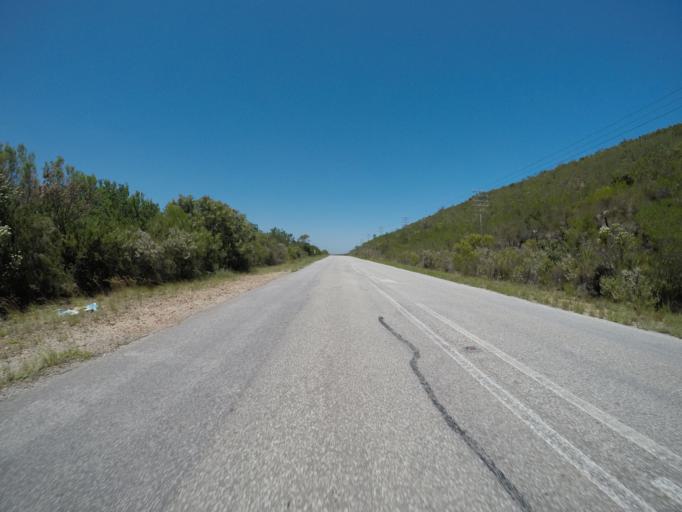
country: ZA
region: Eastern Cape
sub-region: Cacadu District Municipality
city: Kareedouw
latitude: -33.8805
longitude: 24.0585
